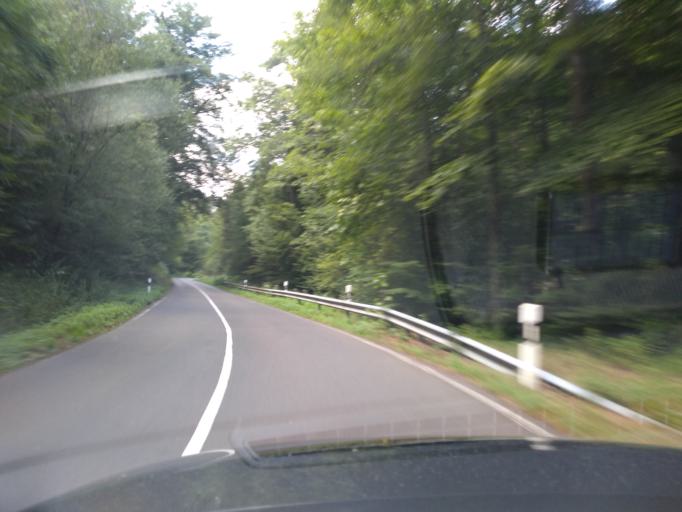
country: DE
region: North Rhine-Westphalia
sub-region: Regierungsbezirk Koln
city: Much
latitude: 50.8416
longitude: 7.4055
